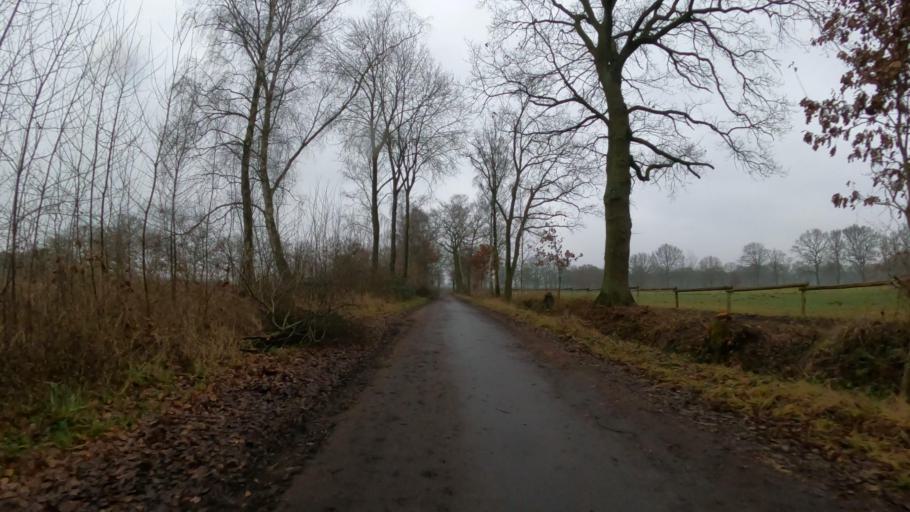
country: DE
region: Schleswig-Holstein
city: Appen
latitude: 53.5963
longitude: 9.7746
